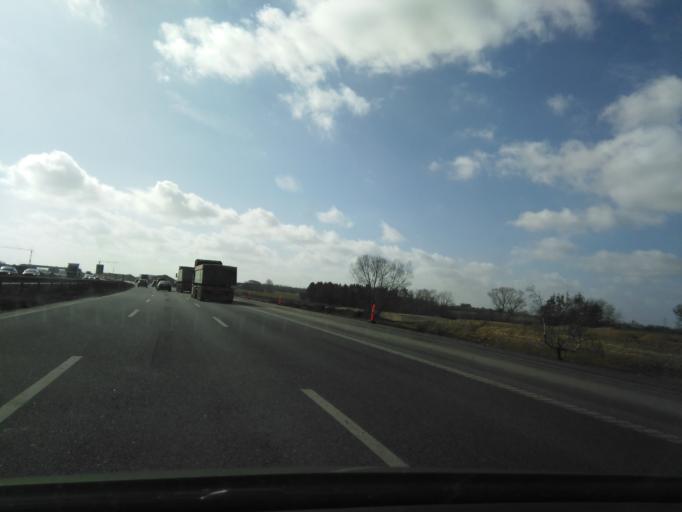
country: DK
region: Zealand
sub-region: Solrod Kommune
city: Solrod
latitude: 55.5112
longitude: 12.1804
